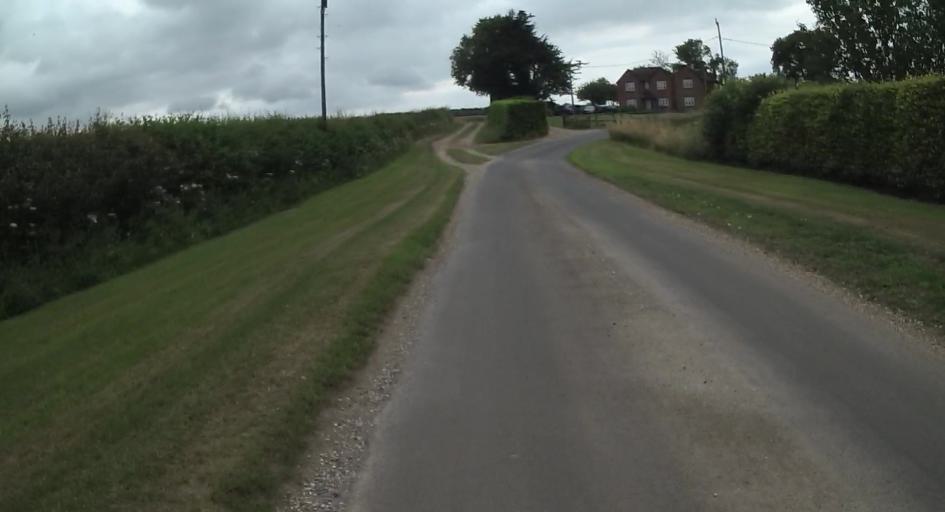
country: GB
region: England
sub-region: Hampshire
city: Swanmore
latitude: 51.0237
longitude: -1.1708
